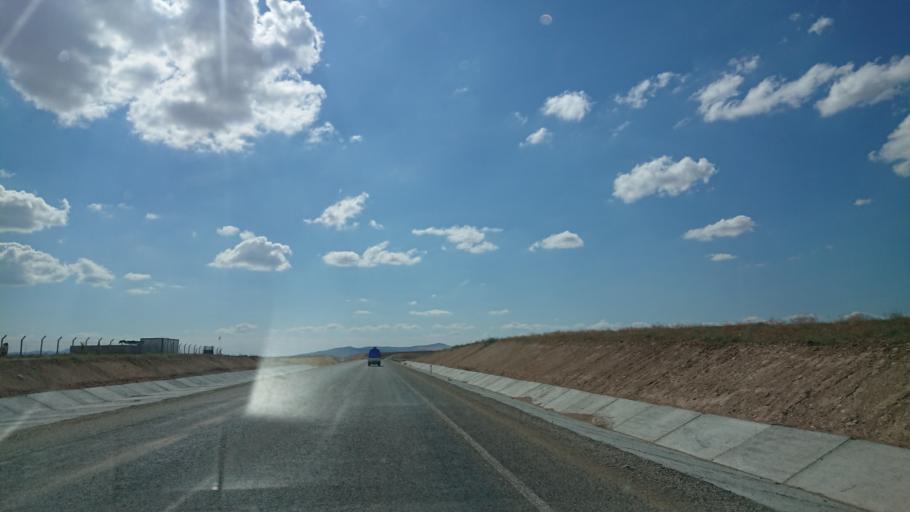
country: TR
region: Kirsehir
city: Kirsehir
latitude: 39.1233
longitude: 33.9969
